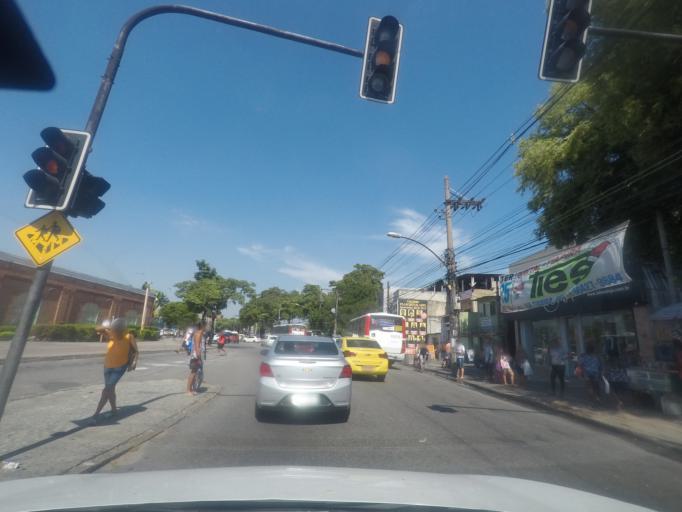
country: BR
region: Rio de Janeiro
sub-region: Nilopolis
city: Nilopolis
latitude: -22.8801
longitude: -43.4671
